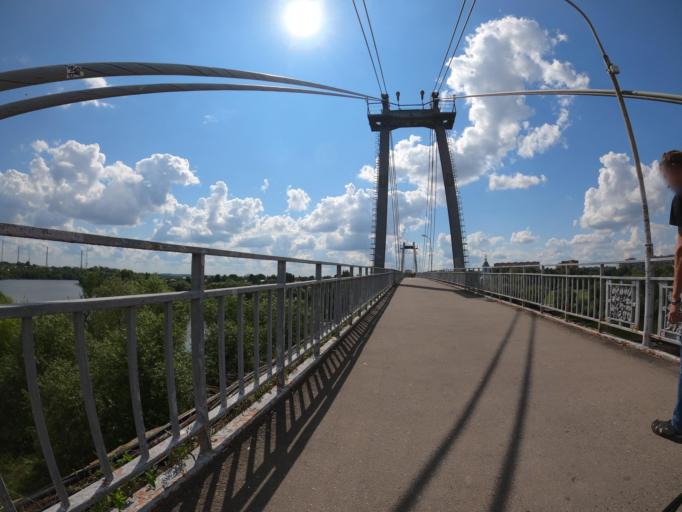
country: RU
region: Moskovskaya
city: Voskresensk
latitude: 55.3185
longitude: 38.6658
